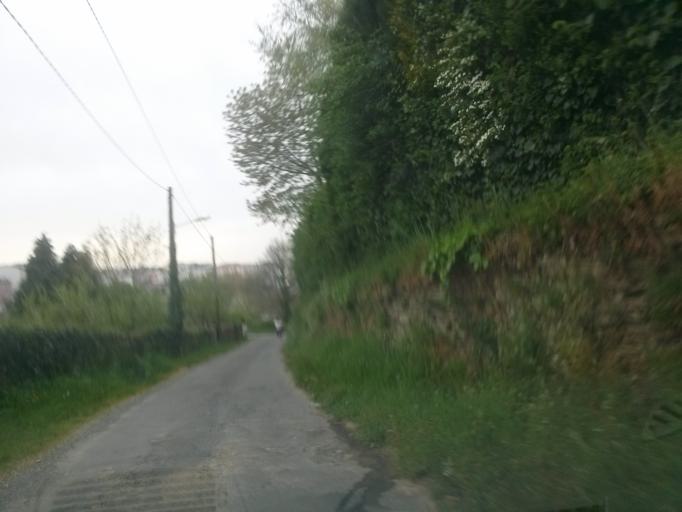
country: ES
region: Galicia
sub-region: Provincia de Lugo
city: Lugo
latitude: 43.0125
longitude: -7.5430
